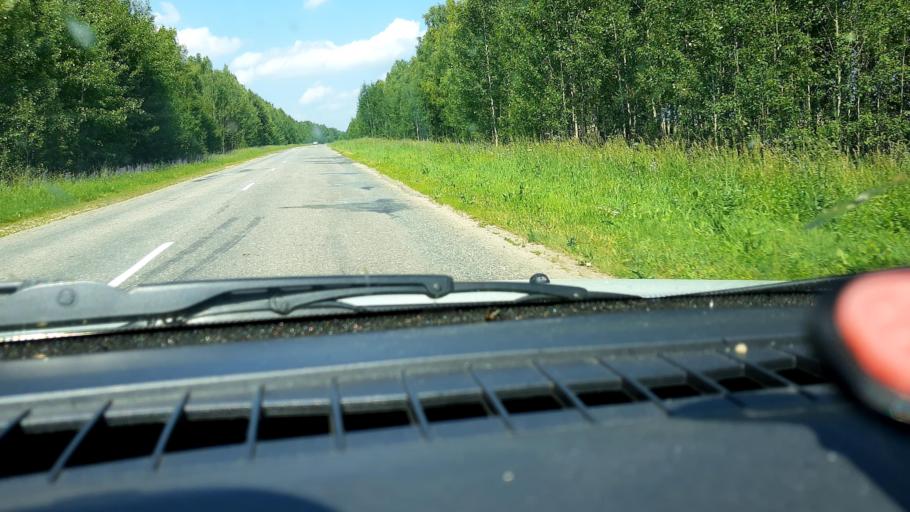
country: RU
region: Nizjnij Novgorod
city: Sharanga
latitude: 57.0616
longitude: 46.5450
